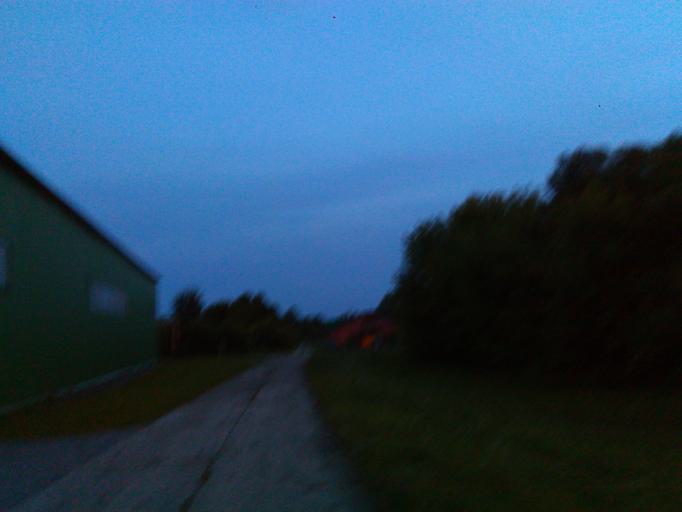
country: RU
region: Penza
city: Lermontovo
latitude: 52.9964
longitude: 43.6771
